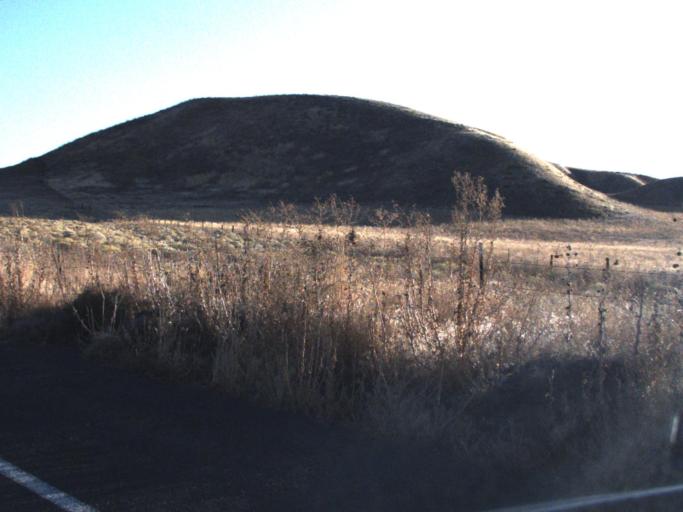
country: US
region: Washington
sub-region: Walla Walla County
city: Waitsburg
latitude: 46.6286
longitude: -118.2408
